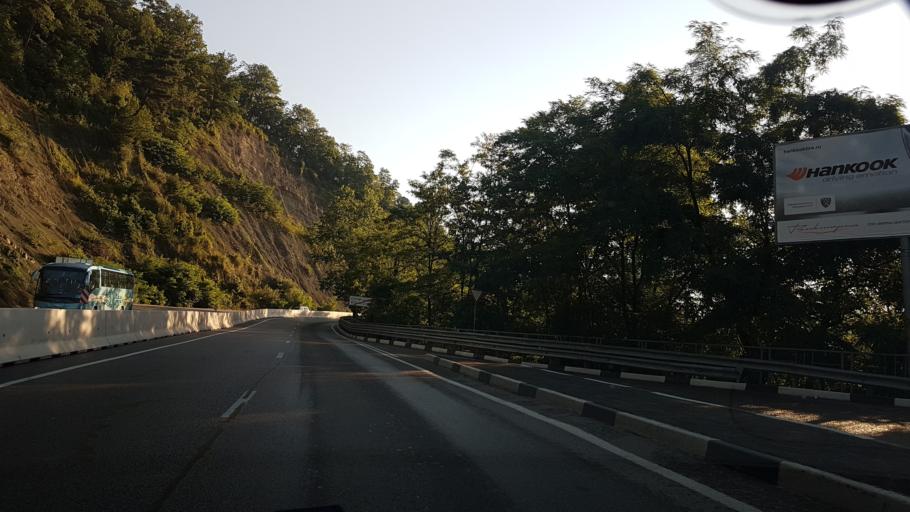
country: RU
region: Krasnodarskiy
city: Dagomys
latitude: 43.6412
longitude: 39.6991
